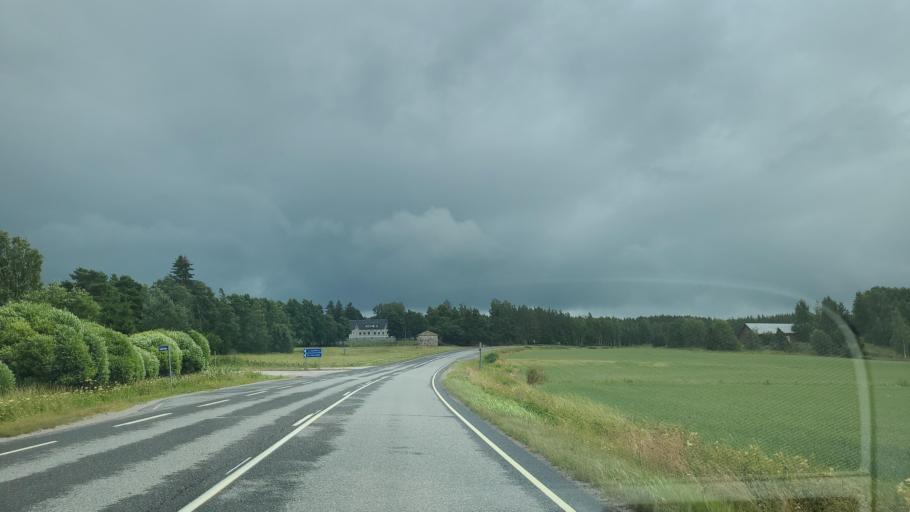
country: FI
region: Varsinais-Suomi
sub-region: Turku
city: Sauvo
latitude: 60.3313
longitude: 22.7120
